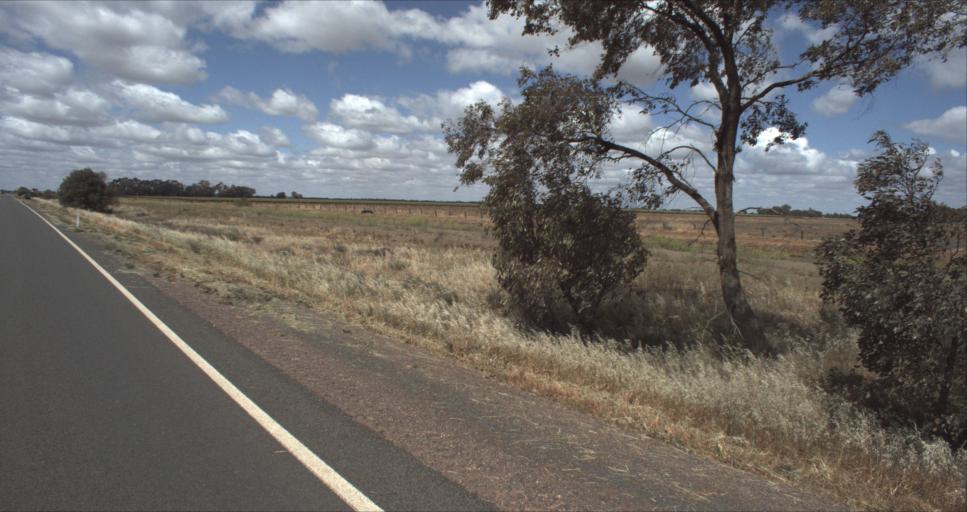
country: AU
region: New South Wales
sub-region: Murrumbidgee Shire
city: Darlington Point
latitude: -34.4781
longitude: 146.1513
